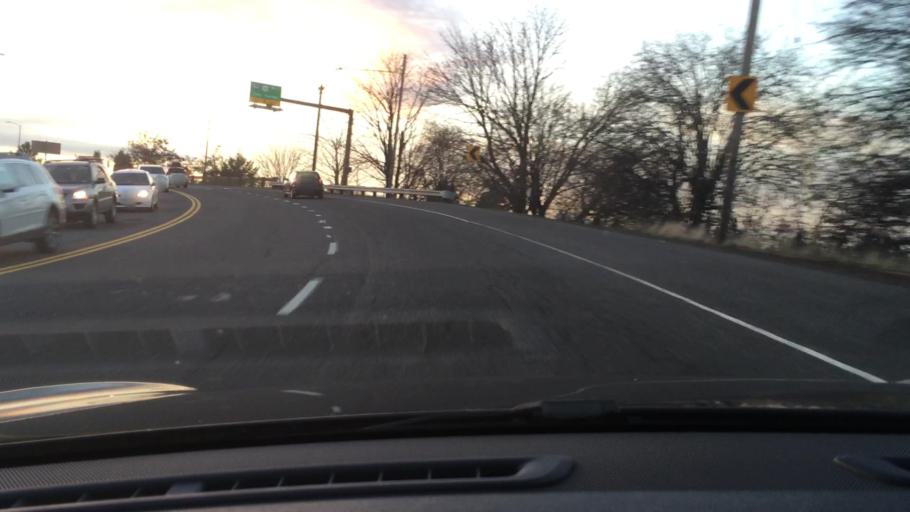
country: US
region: Oregon
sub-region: Multnomah County
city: Lents
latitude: 45.5345
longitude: -122.5778
